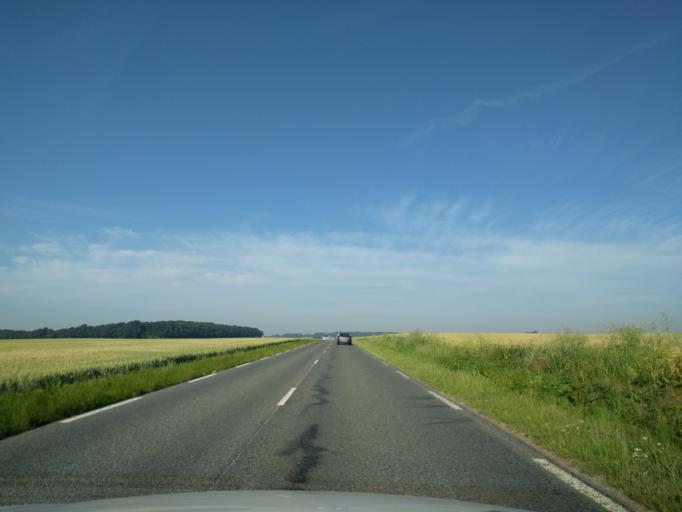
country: FR
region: Picardie
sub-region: Departement de la Somme
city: Montdidier
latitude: 49.6399
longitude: 2.4951
